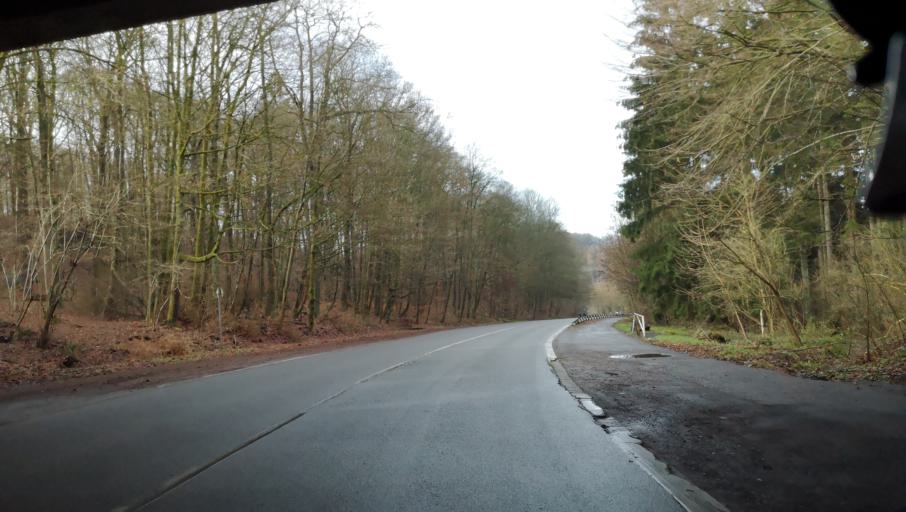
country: DE
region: North Rhine-Westphalia
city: Radevormwald
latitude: 51.1989
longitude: 7.3076
